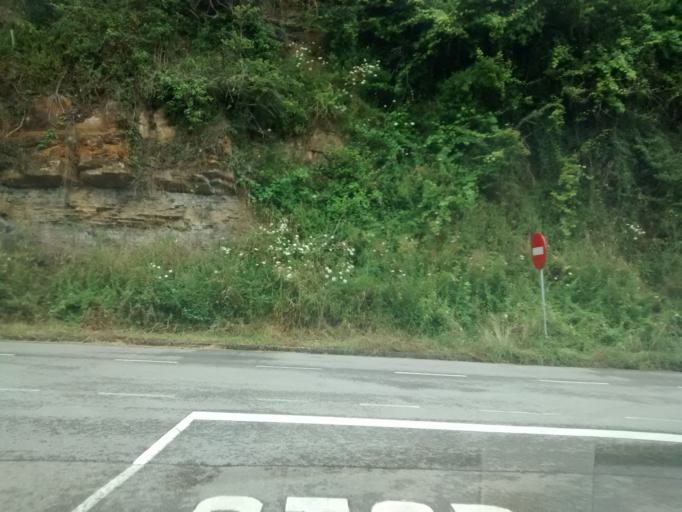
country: ES
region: Asturias
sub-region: Province of Asturias
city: Villaviciosa
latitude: 43.5444
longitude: -5.4036
